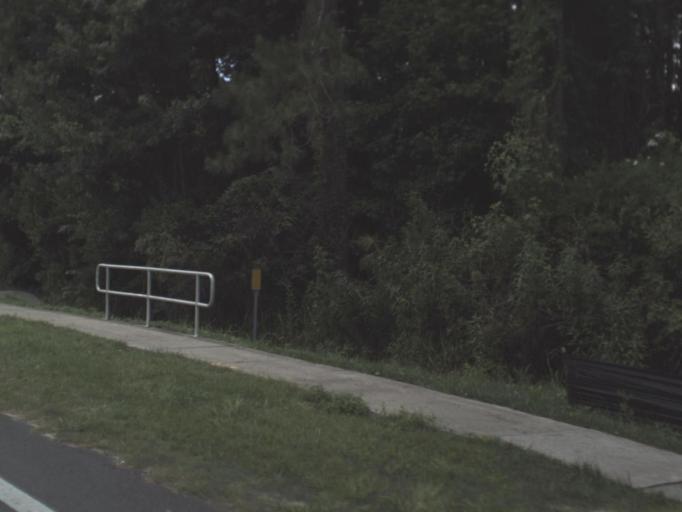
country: US
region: Florida
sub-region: Clay County
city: Keystone Heights
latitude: 29.7149
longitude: -82.0446
